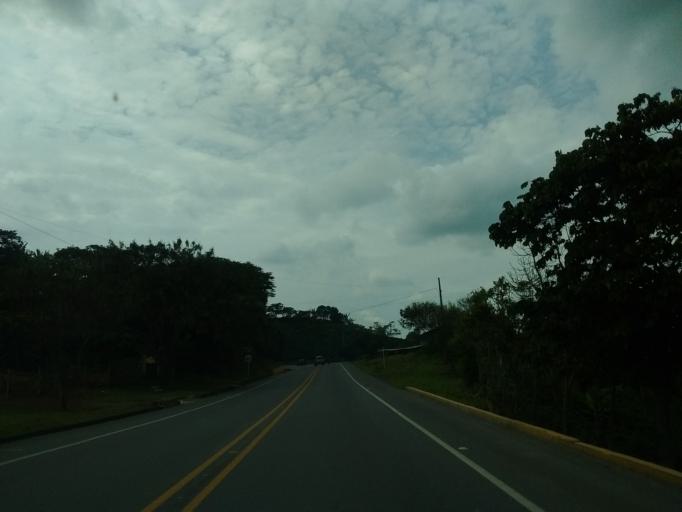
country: CO
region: Cauca
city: Morales
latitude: 2.7759
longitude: -76.5542
